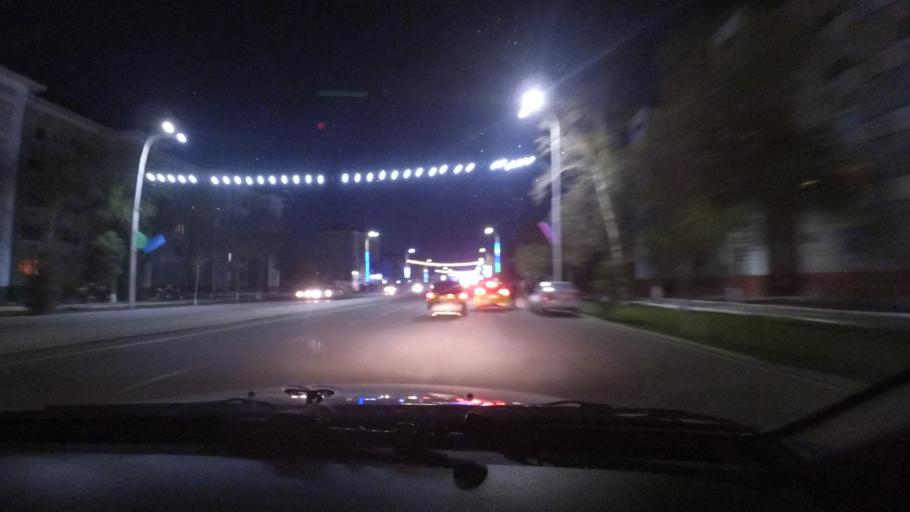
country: UZ
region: Bukhara
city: Bukhara
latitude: 39.7700
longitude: 64.4494
